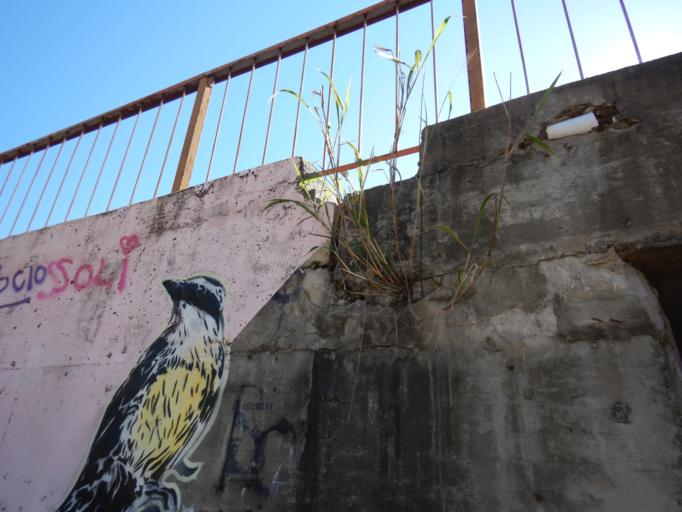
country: AR
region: Santa Fe
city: Santa Fe de la Vera Cruz
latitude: -31.6414
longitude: -60.6267
